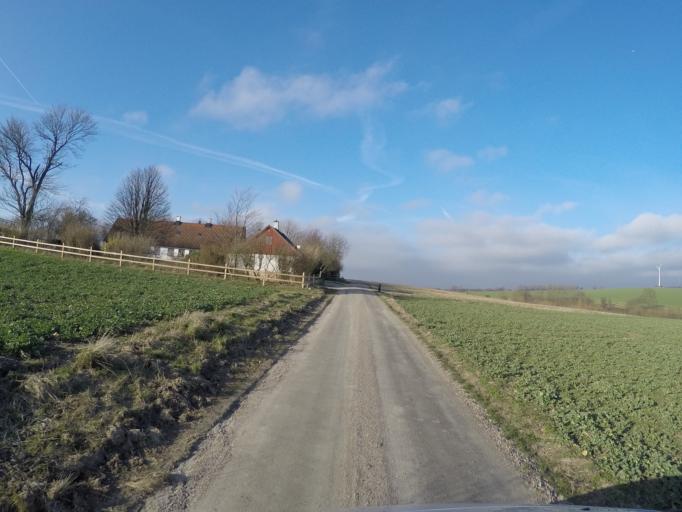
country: SE
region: Skane
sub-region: Lunds Kommun
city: Lund
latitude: 55.6913
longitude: 13.2711
